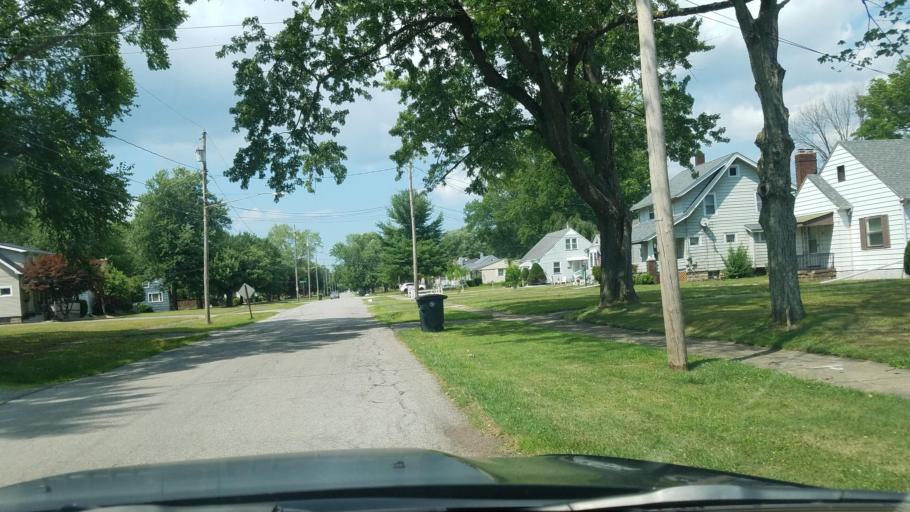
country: US
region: Ohio
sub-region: Trumbull County
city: Bolindale
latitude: 41.2269
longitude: -80.7830
